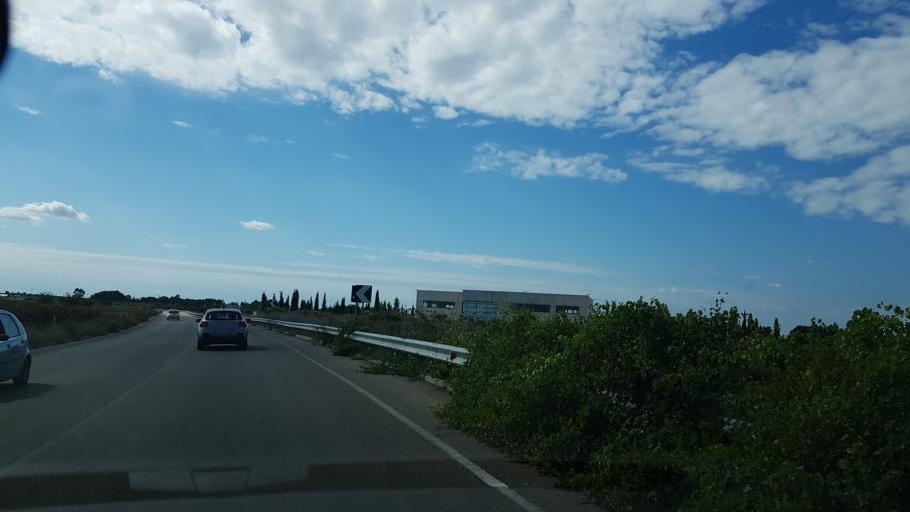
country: IT
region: Apulia
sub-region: Provincia di Lecce
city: Leverano
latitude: 40.2928
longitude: 17.9705
